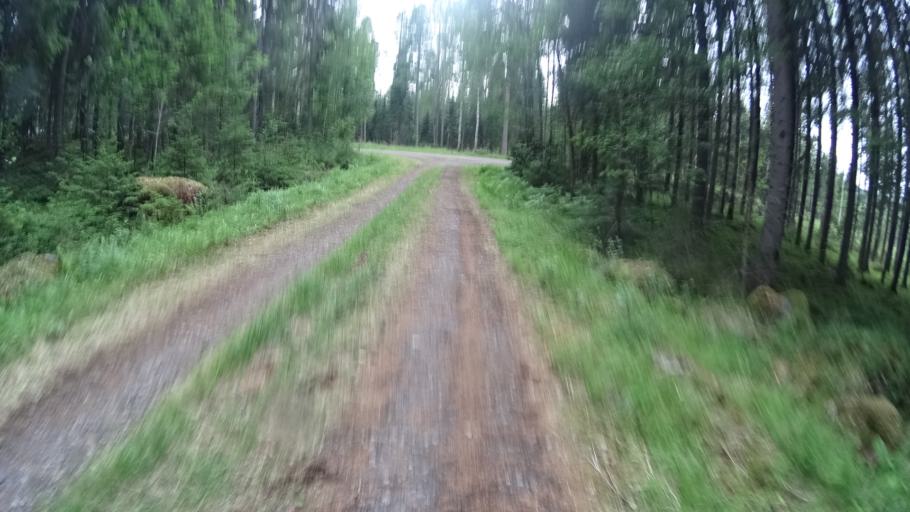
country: FI
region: Uusimaa
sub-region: Helsinki
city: Karkkila
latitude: 60.5825
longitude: 24.1485
